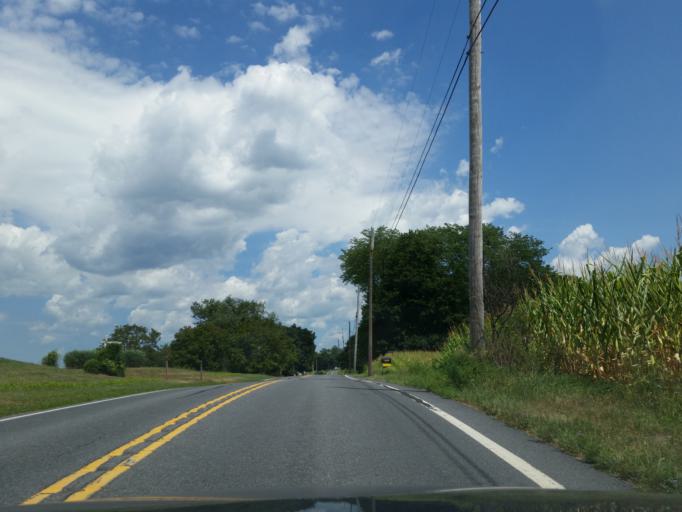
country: US
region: Pennsylvania
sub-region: Lebanon County
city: Annville
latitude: 40.3715
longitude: -76.5087
